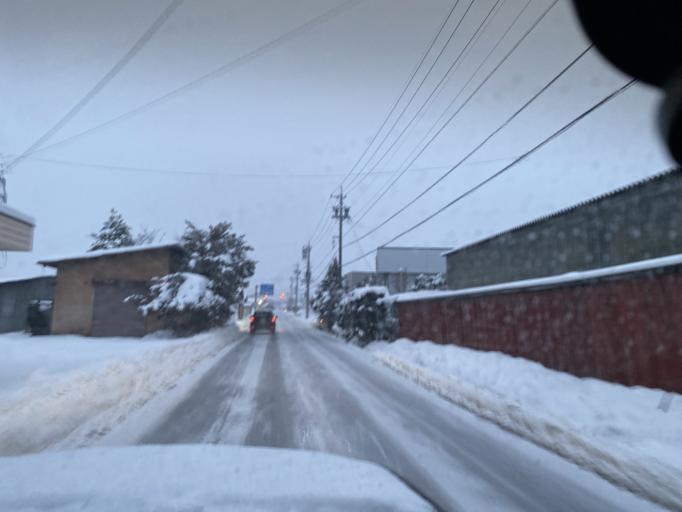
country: JP
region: Nagano
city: Omachi
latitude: 36.5231
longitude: 137.8364
